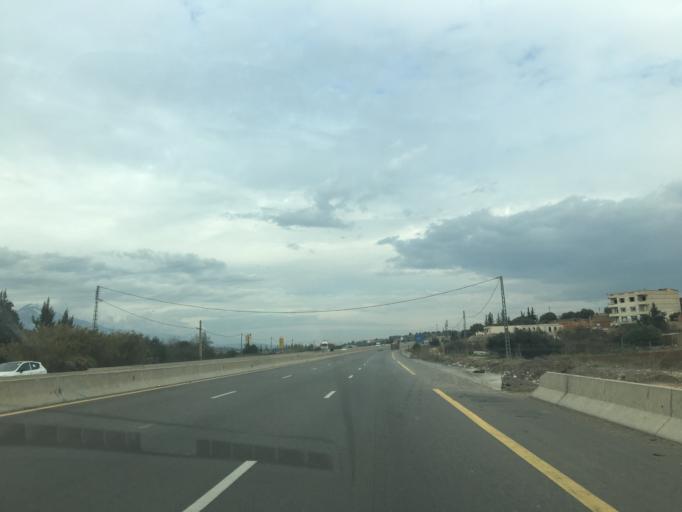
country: DZ
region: Bouira
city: Bouira
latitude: 36.3121
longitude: 4.0499
